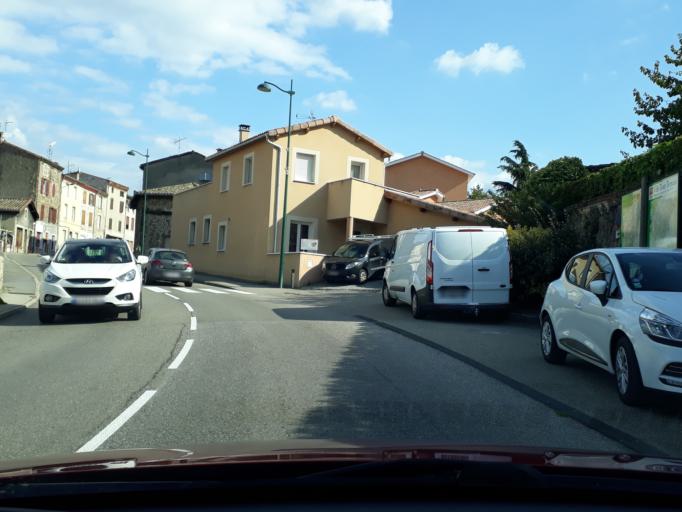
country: FR
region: Rhone-Alpes
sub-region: Departement de la Loire
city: Saint-Pierre-de-Boeuf
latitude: 45.3849
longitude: 4.7472
